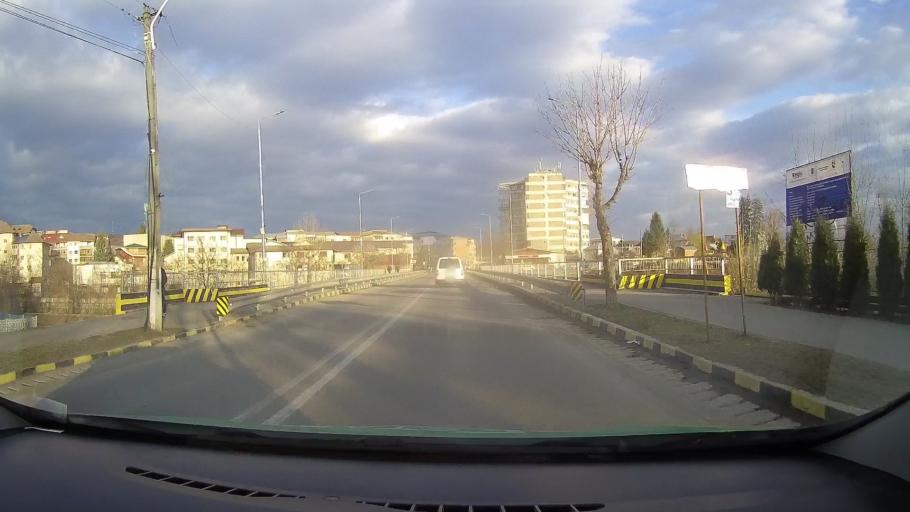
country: RO
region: Dambovita
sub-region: Municipiul Moreni
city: Moreni
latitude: 44.9824
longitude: 25.6427
